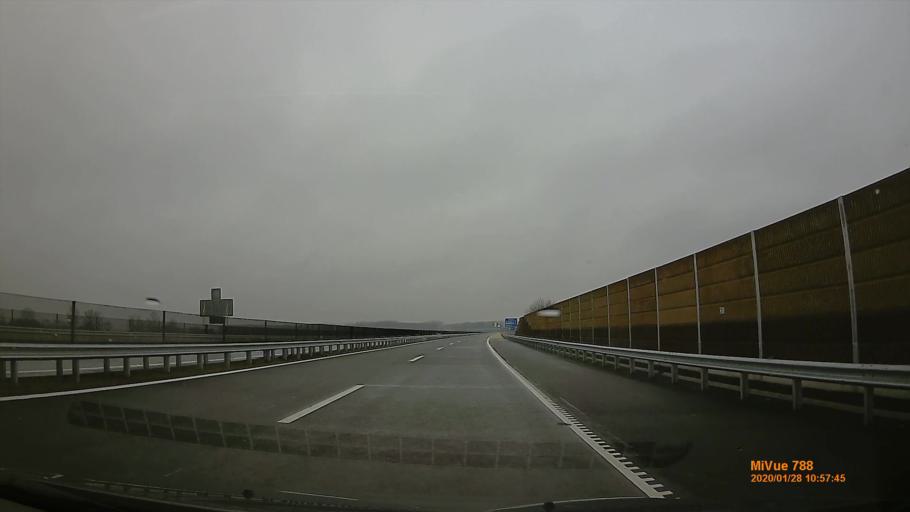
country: HU
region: Pest
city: Peteri
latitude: 47.3730
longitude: 19.4106
